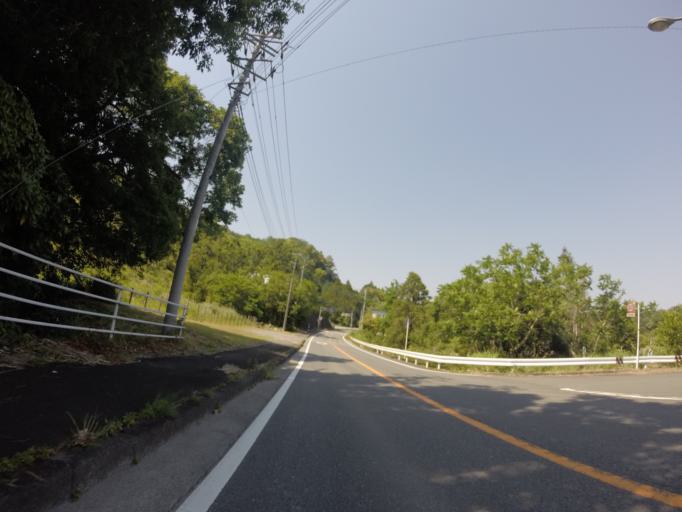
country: JP
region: Shizuoka
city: Fujinomiya
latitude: 35.2001
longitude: 138.5851
